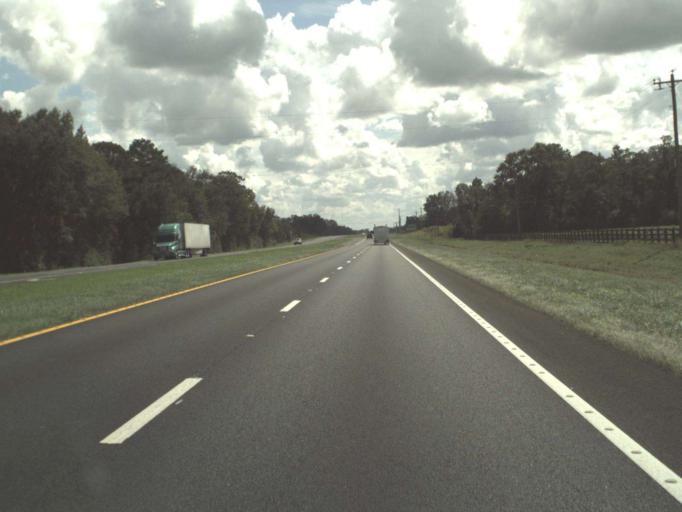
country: US
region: Florida
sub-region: Jackson County
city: Graceville
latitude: 30.9339
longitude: -85.3889
